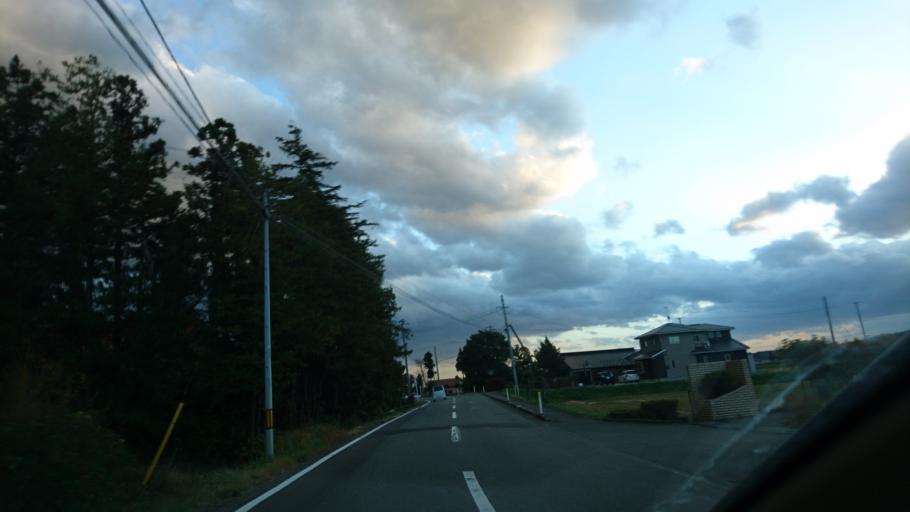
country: JP
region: Iwate
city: Mizusawa
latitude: 39.1127
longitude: 141.1504
